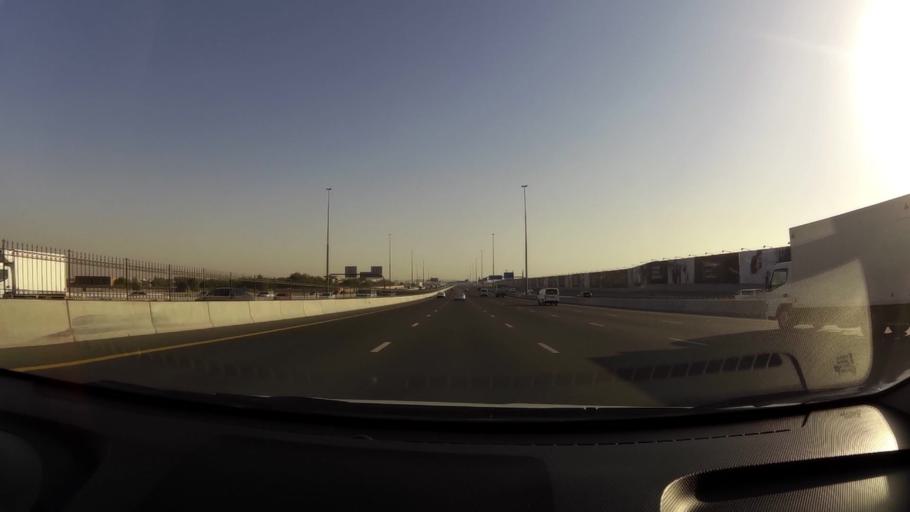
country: AE
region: Ash Shariqah
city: Sharjah
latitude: 25.3315
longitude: 55.4630
